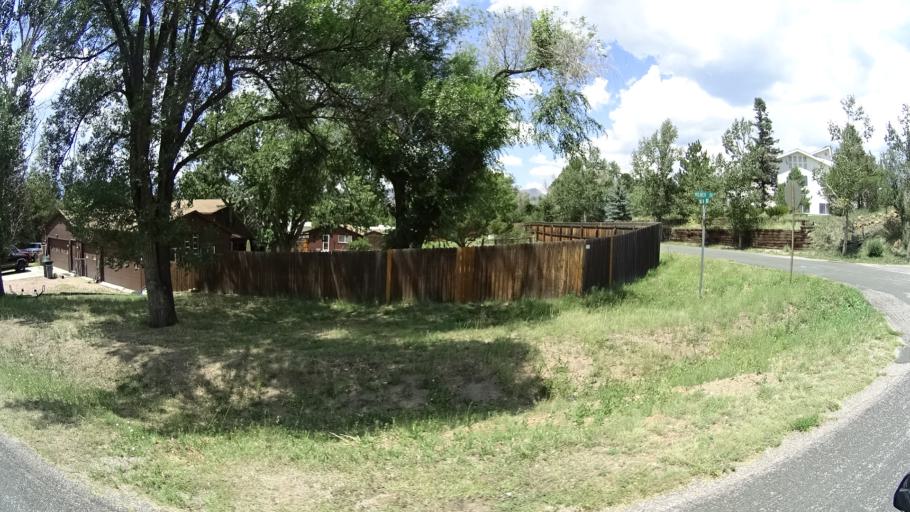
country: US
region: Colorado
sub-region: El Paso County
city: Air Force Academy
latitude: 38.9392
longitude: -104.8049
